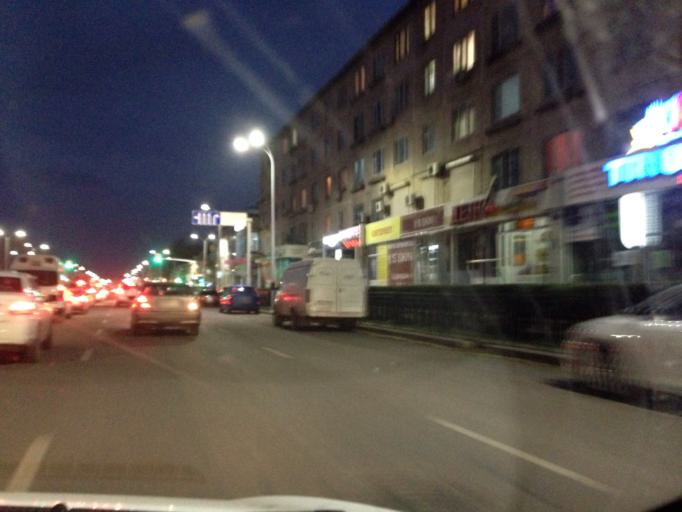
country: KZ
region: Astana Qalasy
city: Astana
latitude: 51.1812
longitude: 71.4172
